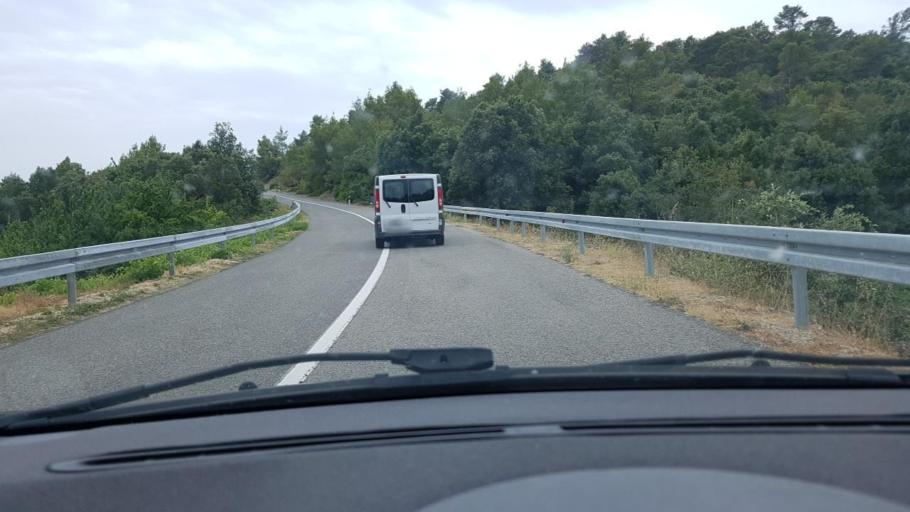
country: HR
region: Dubrovacko-Neretvanska
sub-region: Grad Korcula
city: Zrnovo
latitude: 42.9433
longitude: 17.0247
